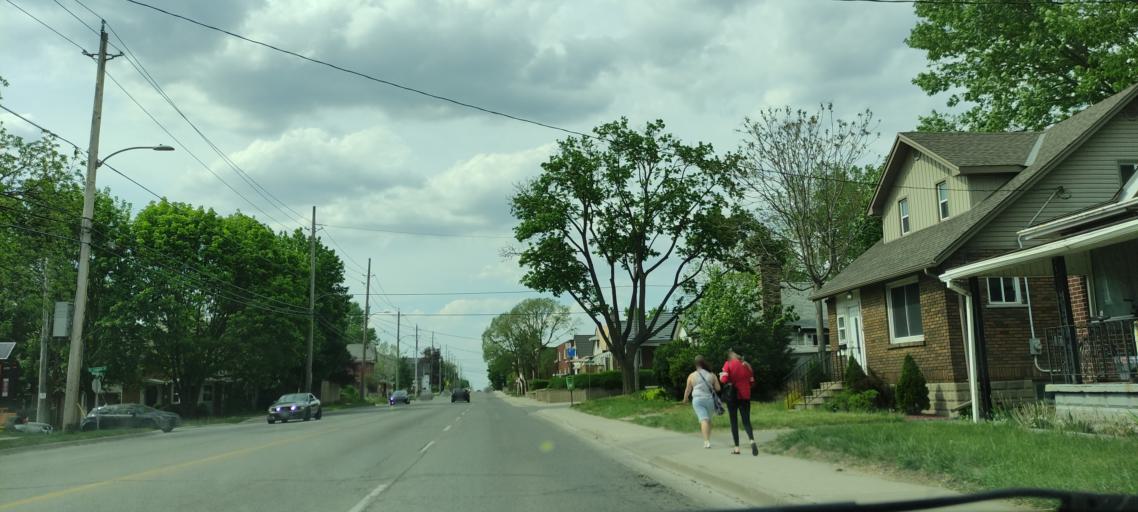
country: CA
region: Ontario
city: London
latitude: 43.0016
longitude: -81.2379
